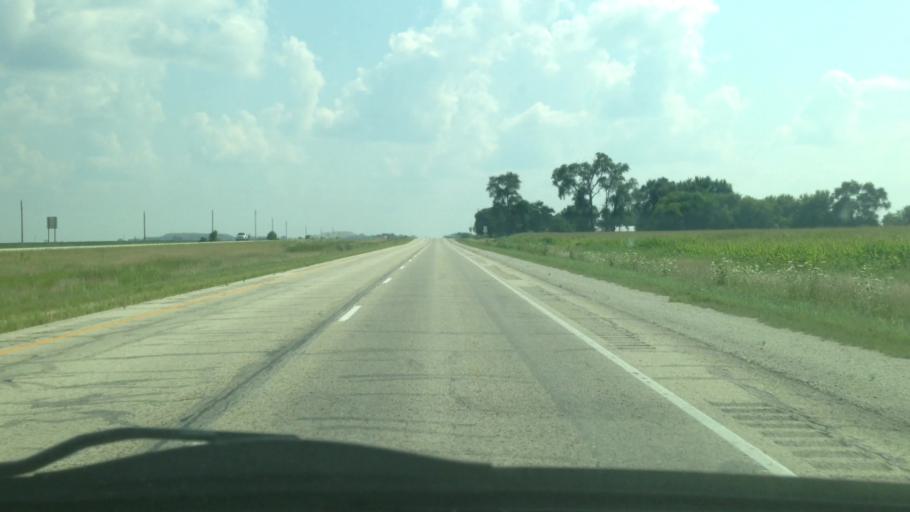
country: US
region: Iowa
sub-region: Bremer County
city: Tripoli
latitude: 42.8537
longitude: -92.3376
